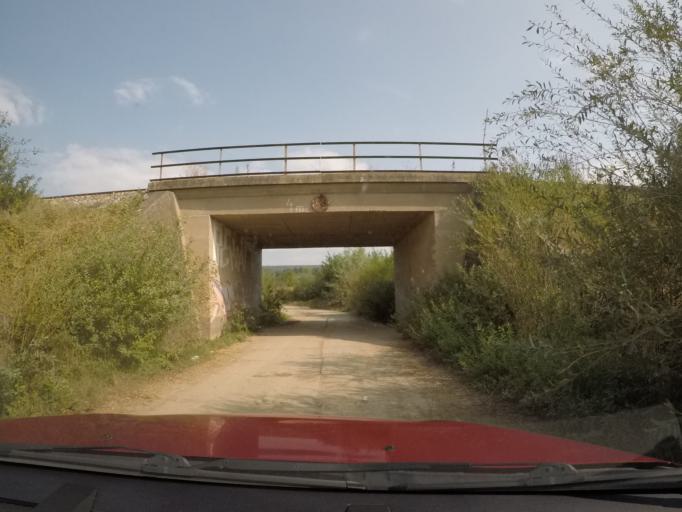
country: SK
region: Kosicky
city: Moldava nad Bodvou
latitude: 48.6073
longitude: 20.9447
